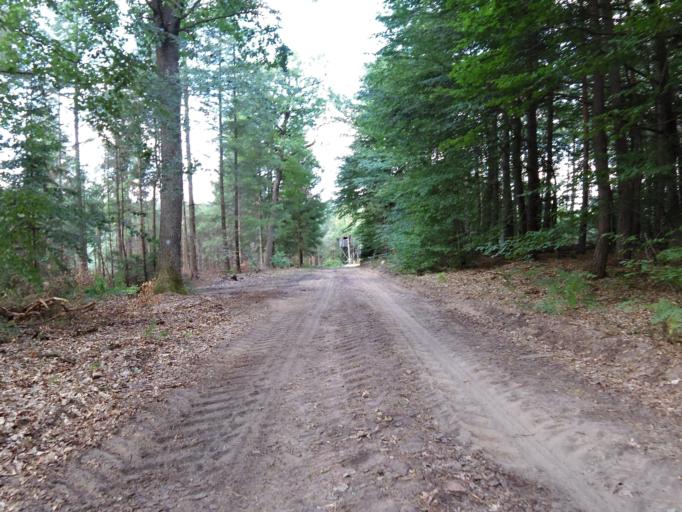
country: DE
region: Rheinland-Pfalz
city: Frankenstein
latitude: 49.4663
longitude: 8.0070
